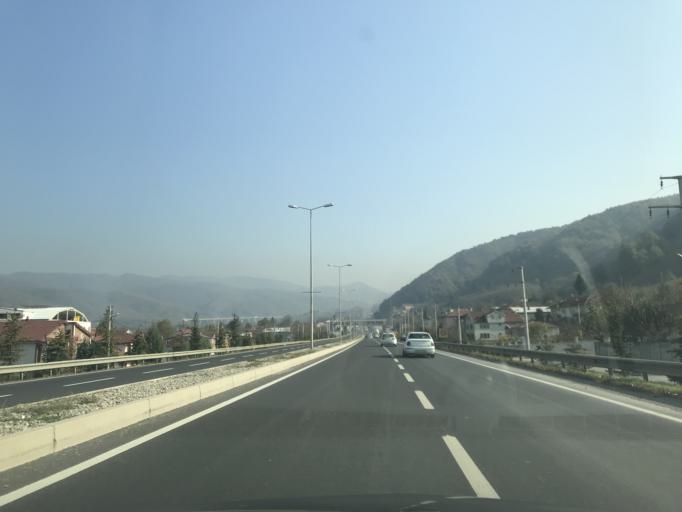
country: TR
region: Duzce
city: Kaynasli
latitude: 40.7729
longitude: 31.3242
